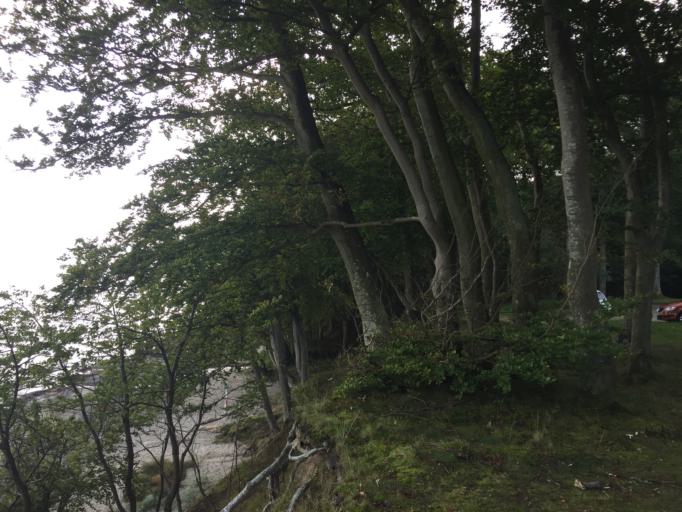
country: DK
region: Zealand
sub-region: Guldborgsund Kommune
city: Stubbekobing
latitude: 54.8124
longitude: 12.1278
